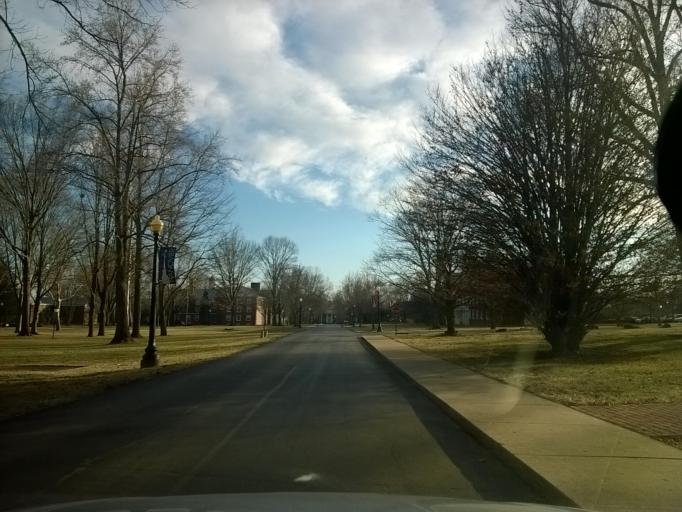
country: US
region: Indiana
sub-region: Jefferson County
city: Hanover
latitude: 38.7166
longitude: -85.4611
